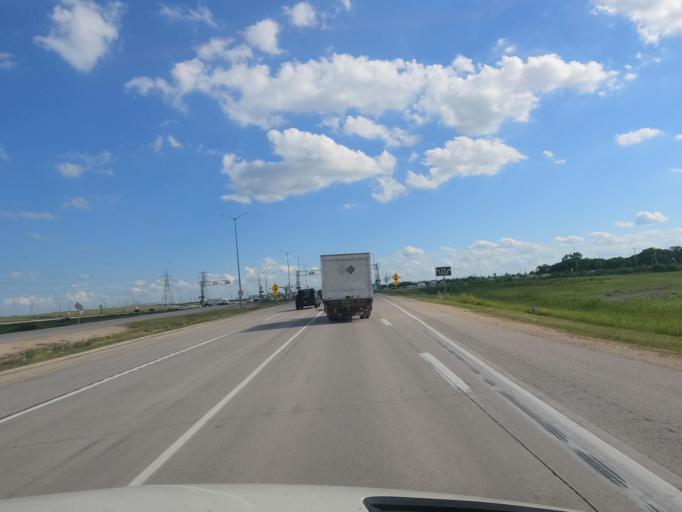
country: CA
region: Manitoba
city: Winnipeg
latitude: 49.8885
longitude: -96.9591
